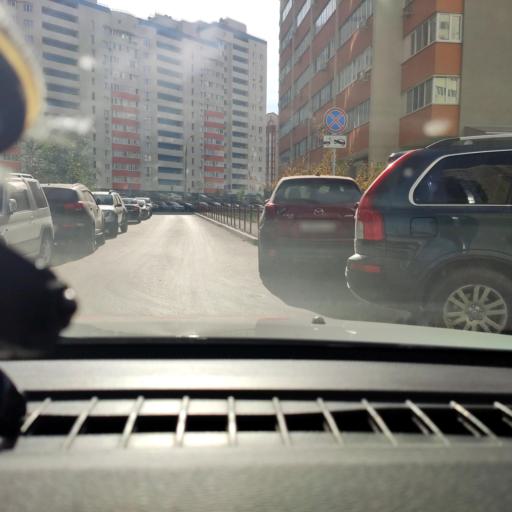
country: RU
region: Samara
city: Samara
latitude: 53.2183
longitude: 50.1700
